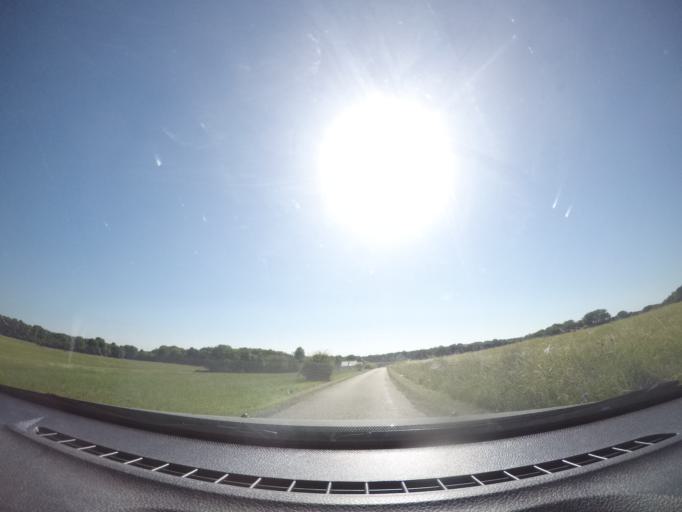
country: BE
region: Wallonia
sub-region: Province de Namur
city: Philippeville
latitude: 50.1740
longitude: 4.5680
